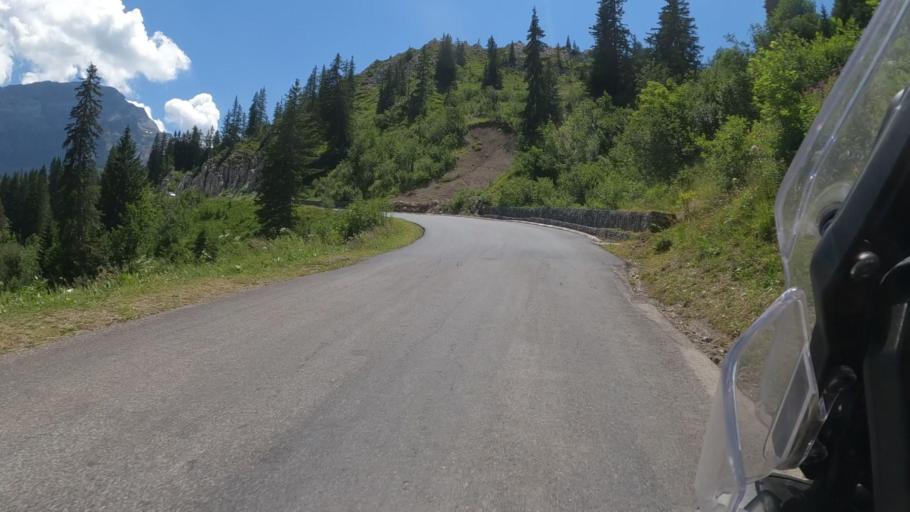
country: CH
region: Vaud
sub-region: Aigle District
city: Villars-sur-Ollon
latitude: 46.3277
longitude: 7.1241
